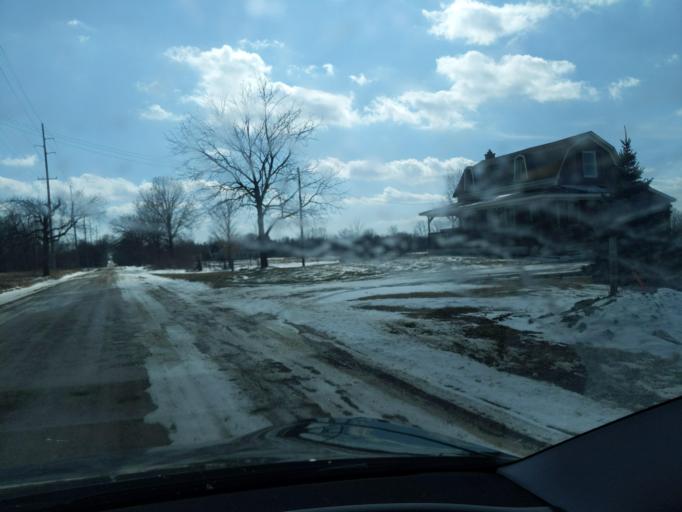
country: US
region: Michigan
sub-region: Livingston County
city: Fowlerville
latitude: 42.6351
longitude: -84.0917
